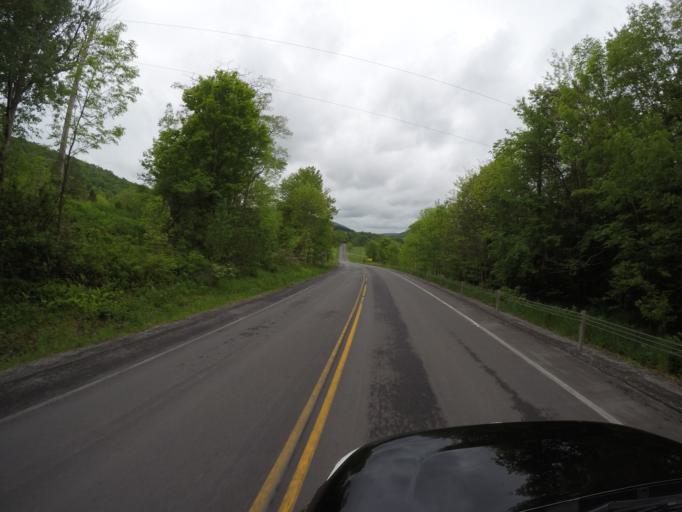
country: US
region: New York
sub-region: Delaware County
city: Delhi
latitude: 42.2444
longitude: -74.8060
